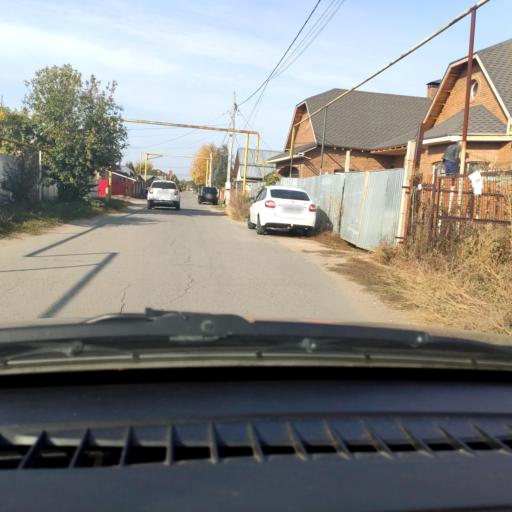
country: RU
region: Samara
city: Podstepki
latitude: 53.5139
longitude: 49.2336
